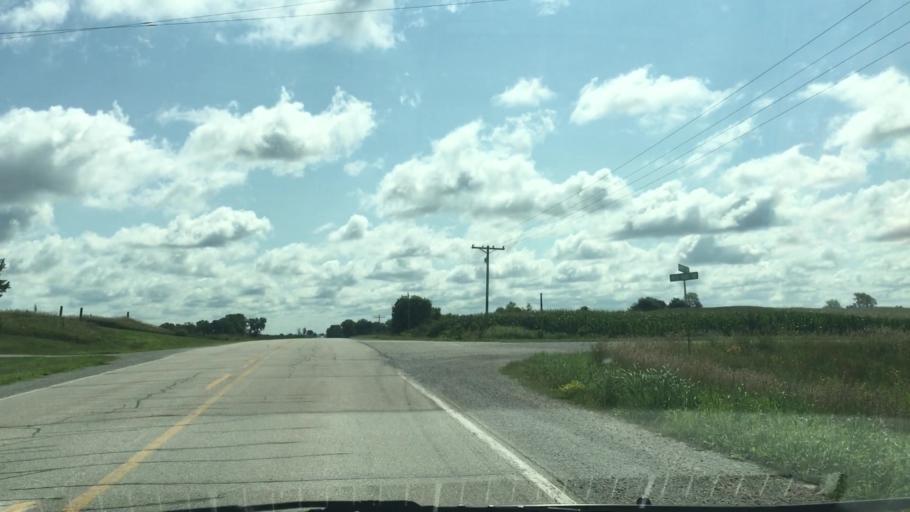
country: US
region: Iowa
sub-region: Johnson County
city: Solon
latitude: 41.8309
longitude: -91.4700
